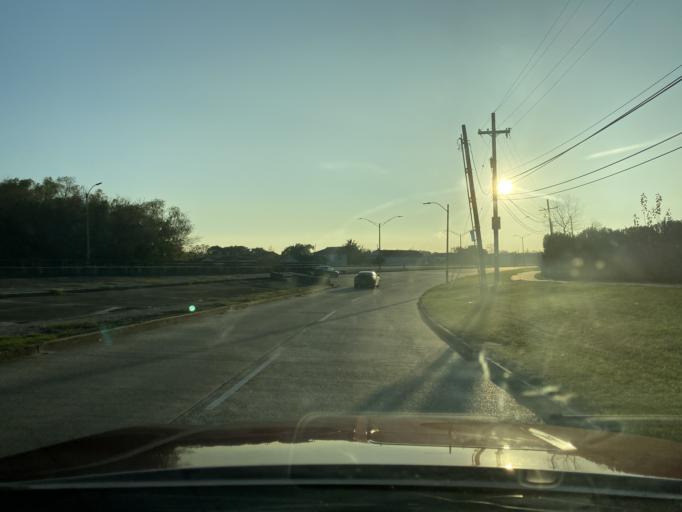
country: US
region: Louisiana
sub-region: Orleans Parish
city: New Orleans
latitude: 30.0278
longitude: -90.0470
